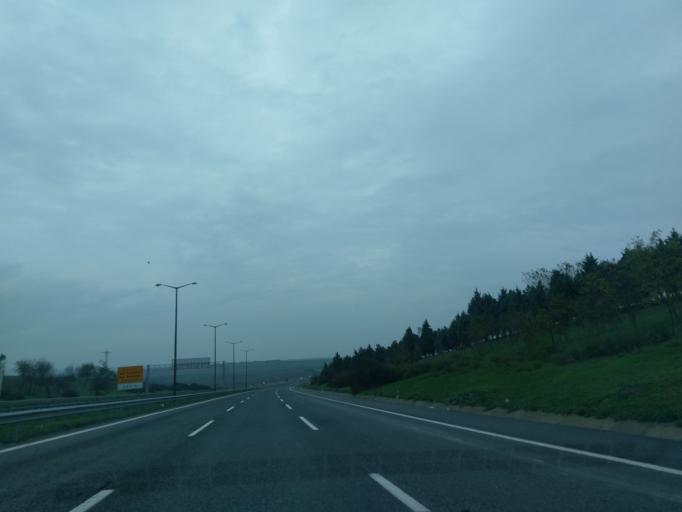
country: TR
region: Istanbul
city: Silivri
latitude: 41.1203
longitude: 28.1792
